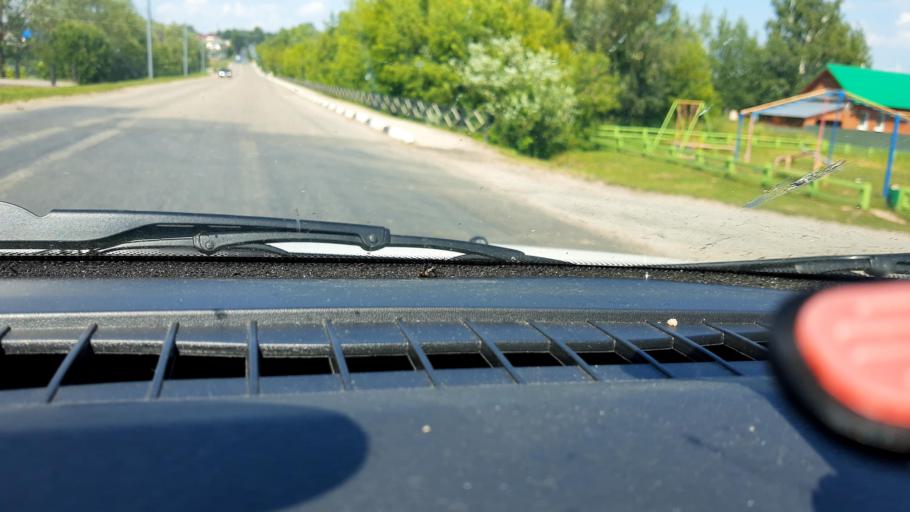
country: RU
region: Nizjnij Novgorod
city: Sharanga
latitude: 57.1673
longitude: 46.5405
